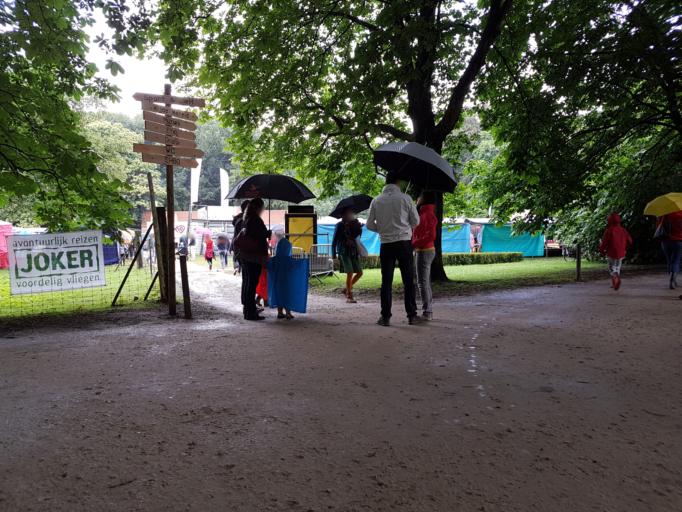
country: BE
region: Flanders
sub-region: Provincie Antwerpen
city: Mechelen
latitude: 51.0467
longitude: 4.4723
